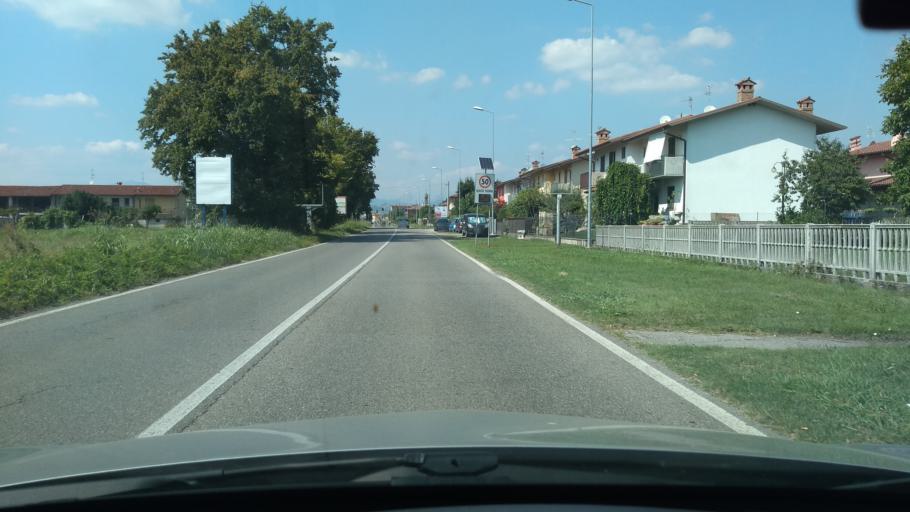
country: IT
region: Lombardy
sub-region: Provincia di Bergamo
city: Zanica
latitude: 45.6315
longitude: 9.6869
